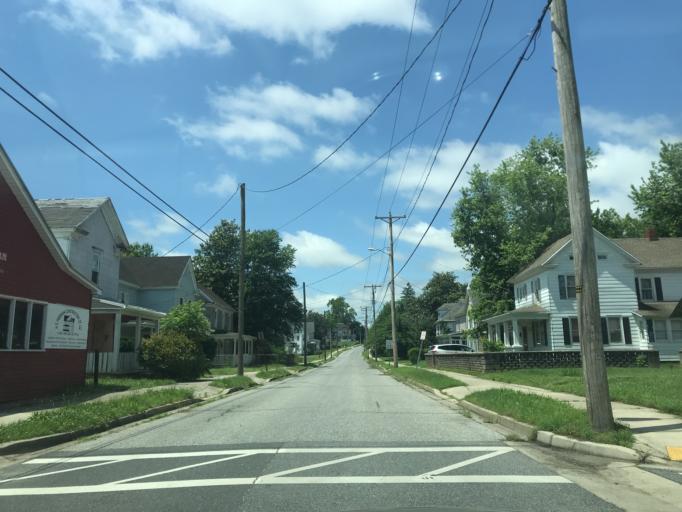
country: US
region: Maryland
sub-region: Caroline County
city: Federalsburg
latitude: 38.6919
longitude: -75.7740
